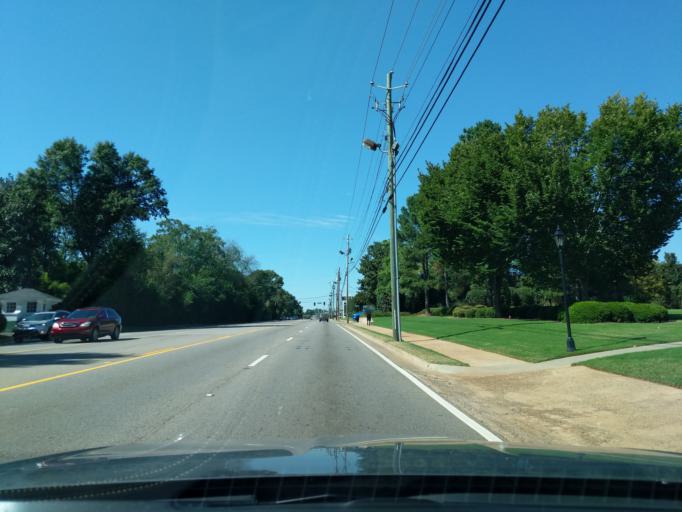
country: US
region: South Carolina
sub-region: Aiken County
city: North Augusta
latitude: 33.5054
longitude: -82.0175
